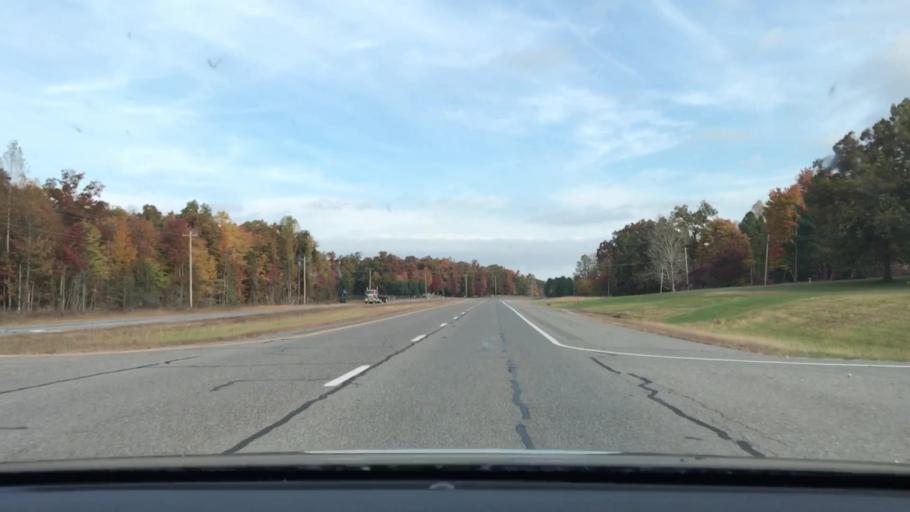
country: US
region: Tennessee
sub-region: Fentress County
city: Jamestown
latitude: 36.3717
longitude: -84.9439
